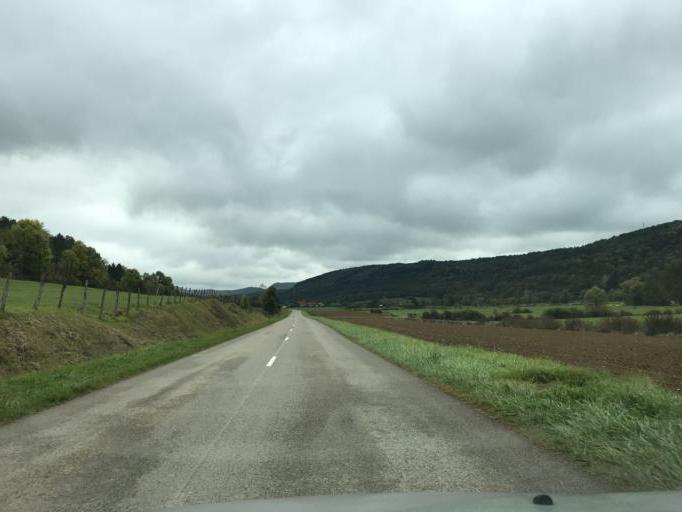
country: FR
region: Rhone-Alpes
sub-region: Departement de l'Ain
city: Coligny
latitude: 46.3831
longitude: 5.4449
